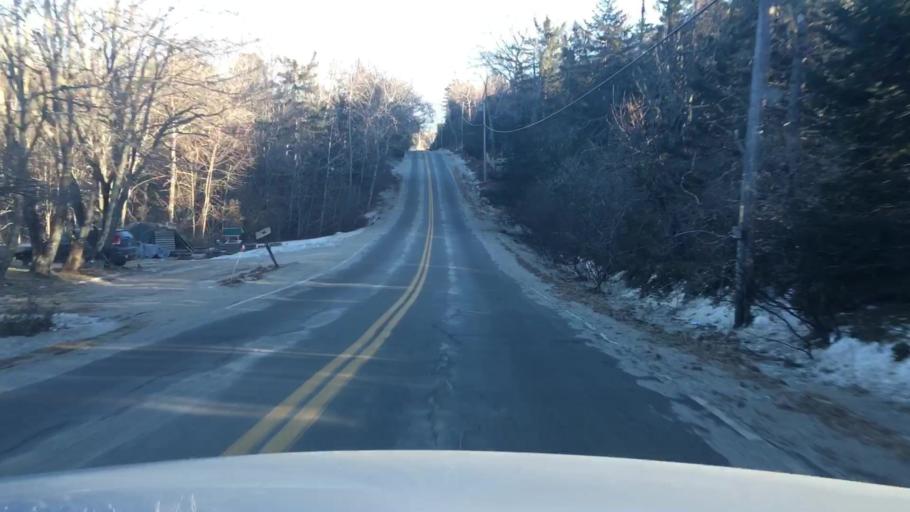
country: US
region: Maine
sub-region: Hancock County
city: Penobscot
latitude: 44.3901
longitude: -68.7045
